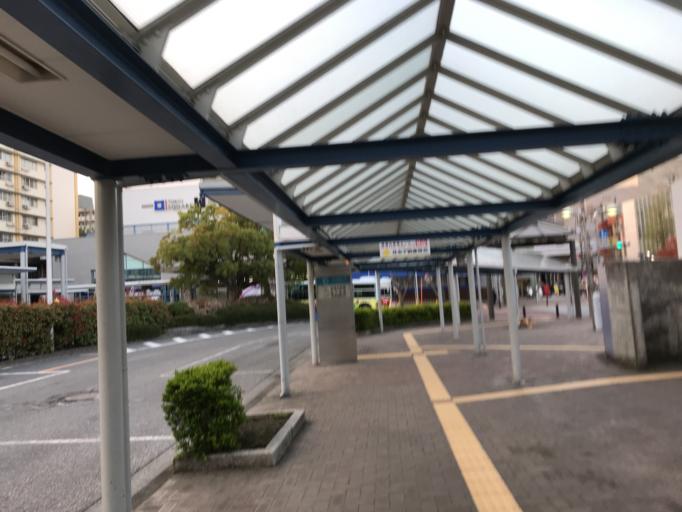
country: JP
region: Tokyo
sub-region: Machida-shi
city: Machida
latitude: 35.5439
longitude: 139.5167
